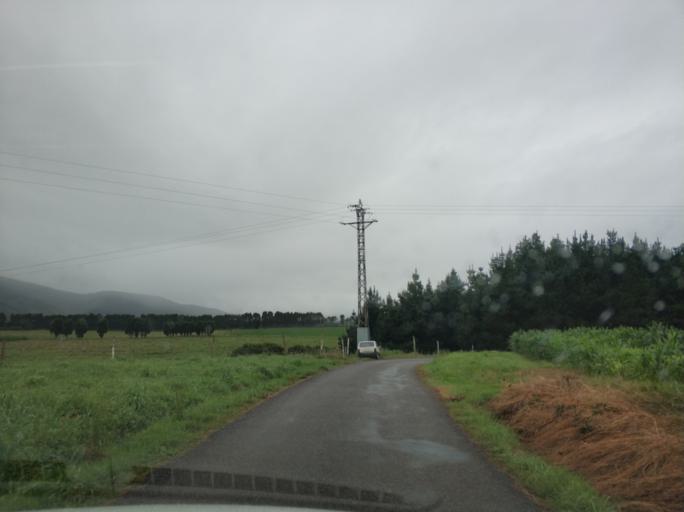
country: ES
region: Asturias
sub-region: Province of Asturias
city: Tineo
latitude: 43.5582
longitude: -6.4658
